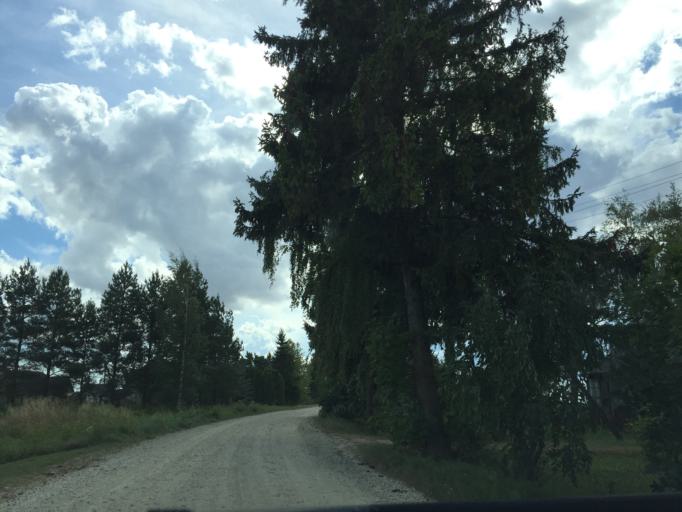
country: LT
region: Siauliu apskritis
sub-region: Joniskis
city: Joniskis
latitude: 56.3419
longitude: 23.6215
